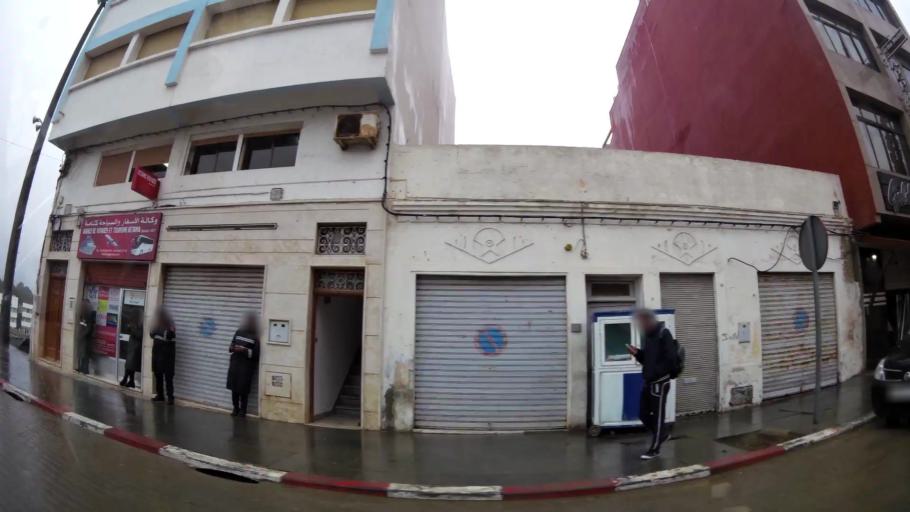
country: MA
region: Taza-Al Hoceima-Taounate
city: Al Hoceima
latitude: 35.2445
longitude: -3.9295
